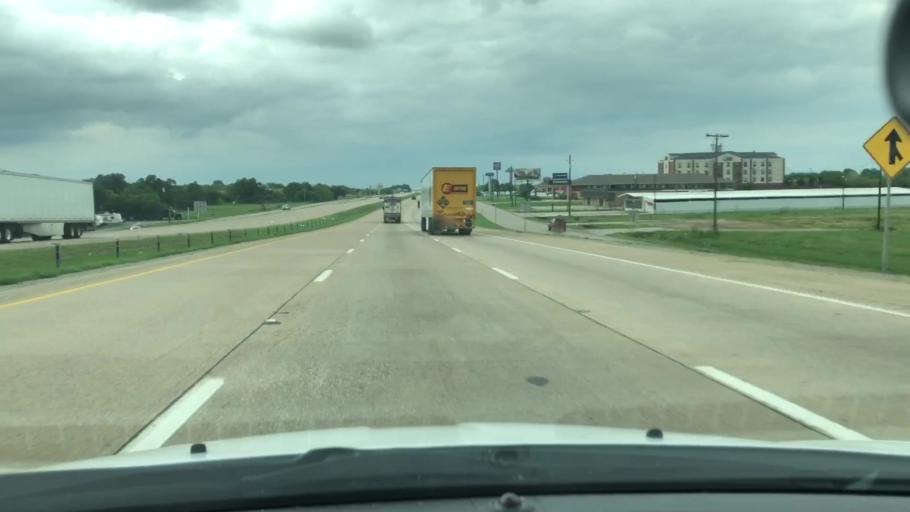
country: US
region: Texas
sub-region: Ellis County
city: Ennis
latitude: 32.3359
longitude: -96.6167
